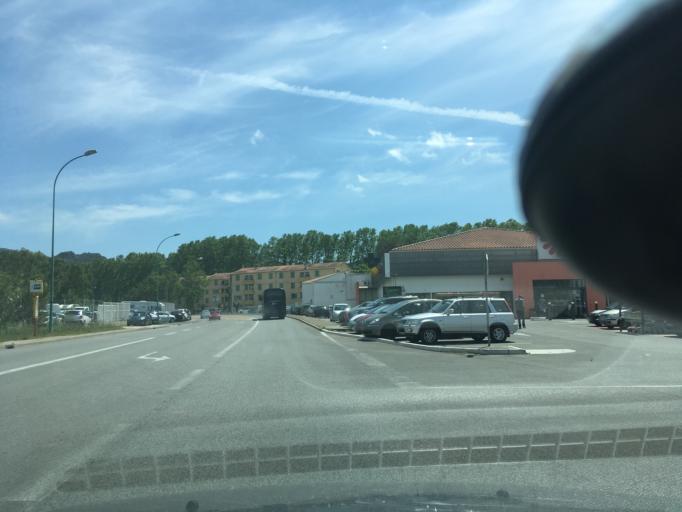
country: FR
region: Provence-Alpes-Cote d'Azur
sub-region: Departement du Var
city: Le Muy
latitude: 43.4735
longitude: 6.5709
